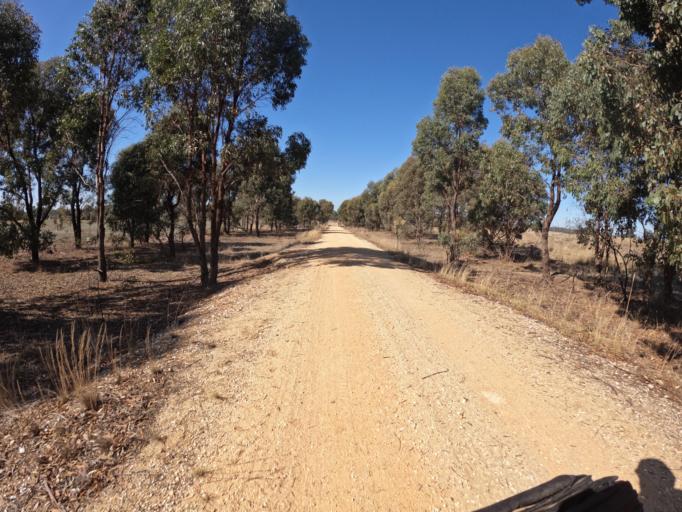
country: AU
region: Victoria
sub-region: Greater Bendigo
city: Kennington
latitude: -36.8223
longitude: 144.5797
